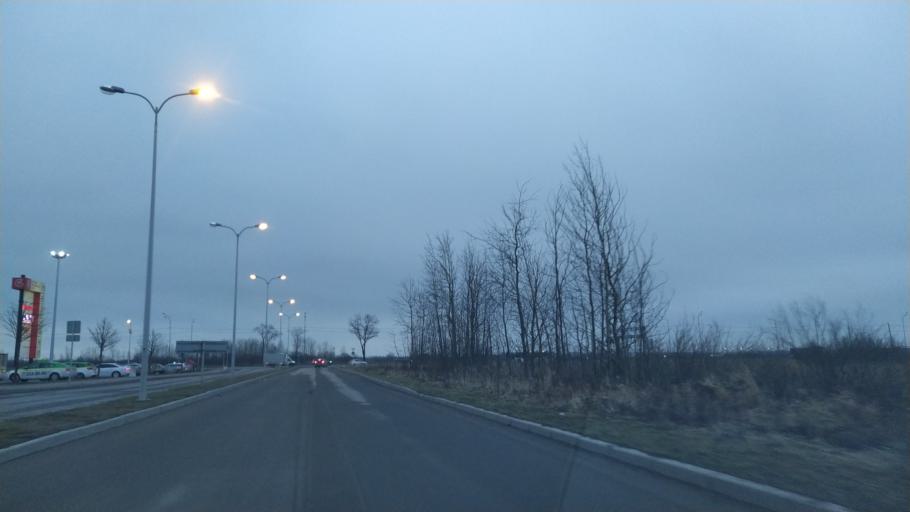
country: RU
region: St.-Petersburg
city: Aleksandrovskaya
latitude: 59.7874
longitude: 30.3218
